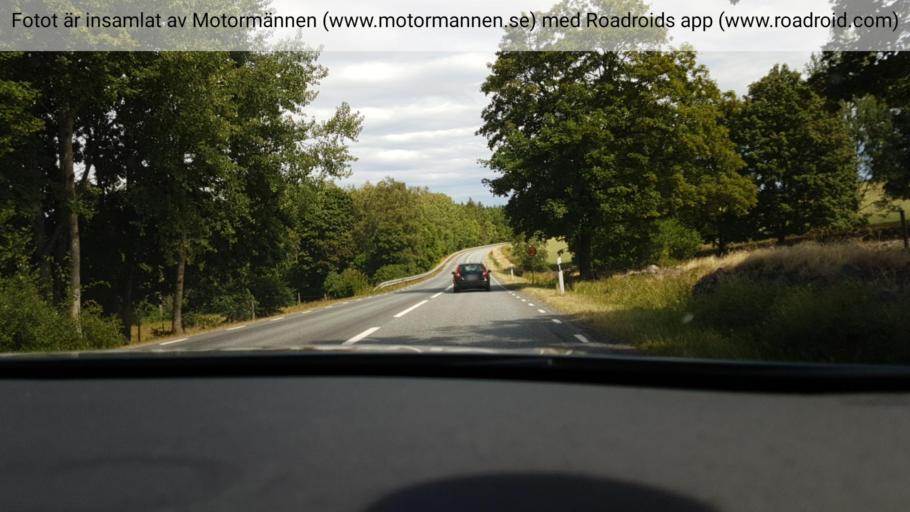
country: SE
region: Joenkoeping
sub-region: Tranas Kommun
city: Tranas
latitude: 57.9966
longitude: 14.8635
